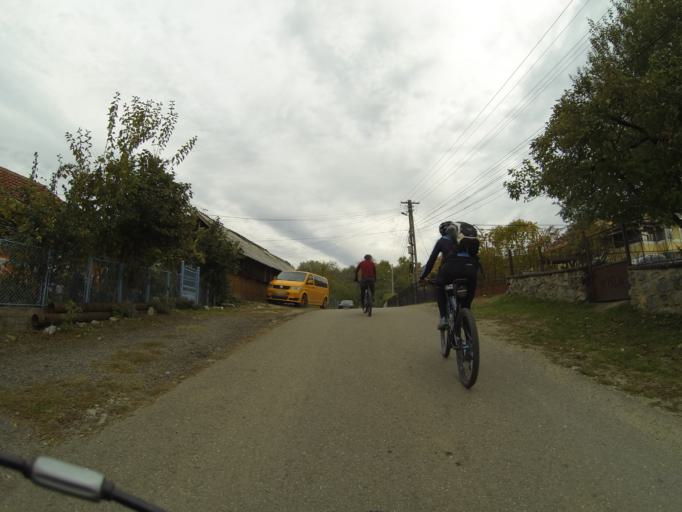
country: RO
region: Gorj
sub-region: Comuna Tismana
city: Sohodol
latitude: 45.0508
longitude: 22.8968
